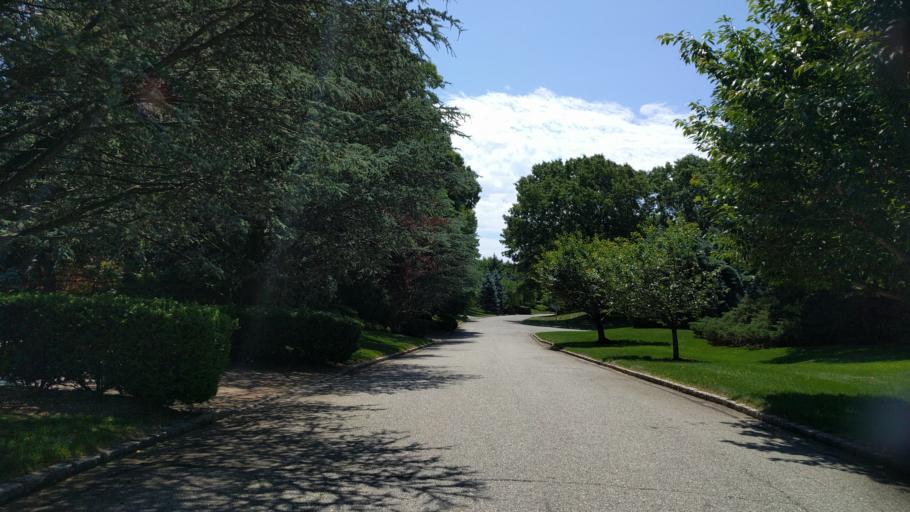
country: US
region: New York
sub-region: Nassau County
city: Oyster Bay
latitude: 40.8664
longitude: -73.5369
